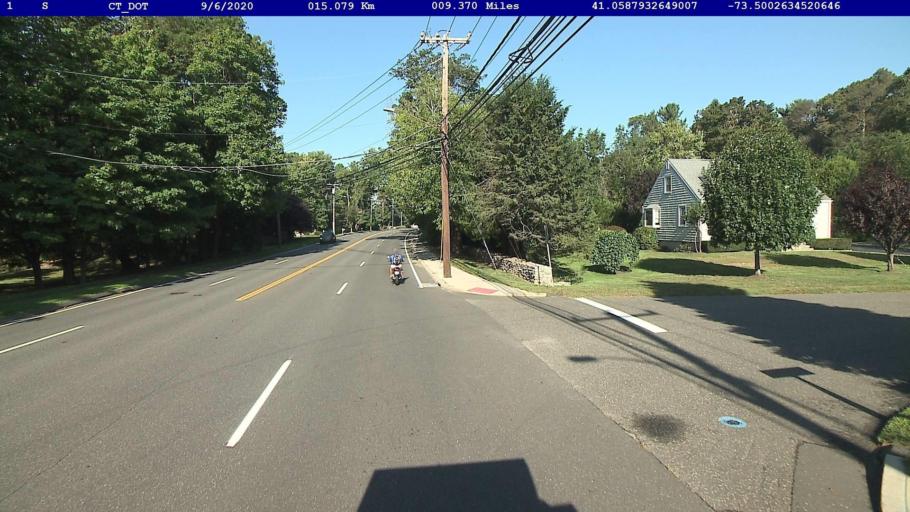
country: US
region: Connecticut
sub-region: Fairfield County
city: Darien
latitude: 41.0589
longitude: -73.5003
